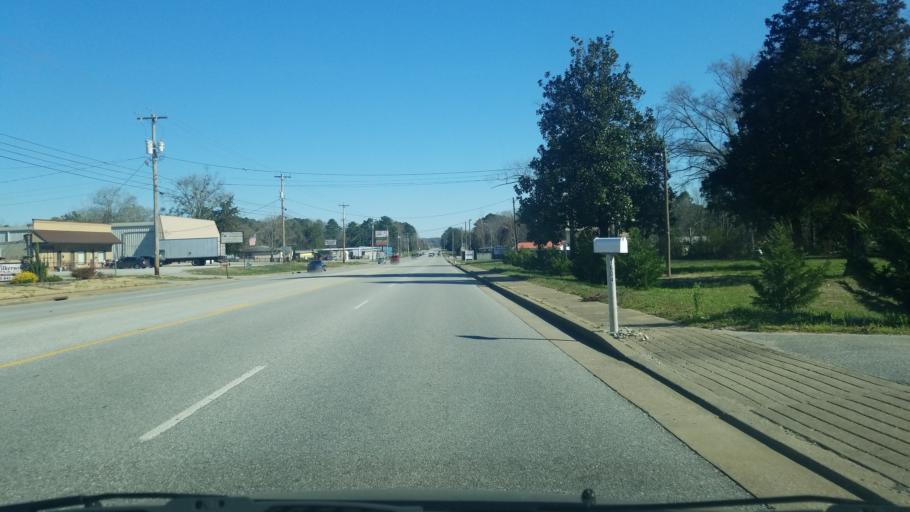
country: US
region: Tennessee
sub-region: Hamilton County
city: Middle Valley
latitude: 35.1744
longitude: -85.1722
